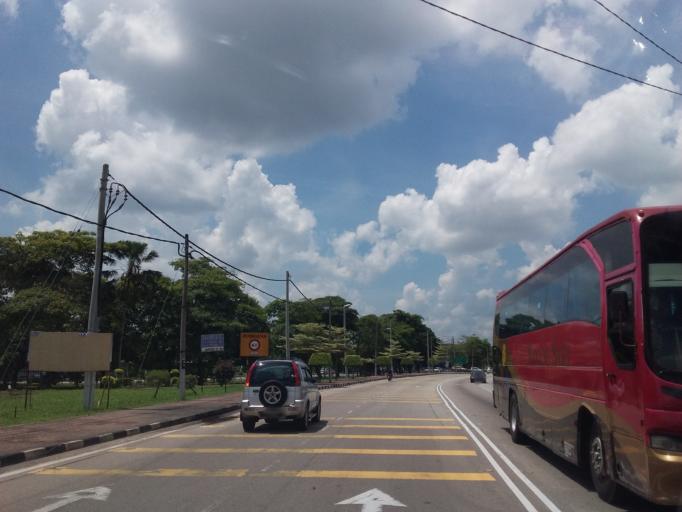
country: MY
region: Johor
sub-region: Daerah Batu Pahat
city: Batu Pahat
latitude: 1.8595
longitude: 102.9272
